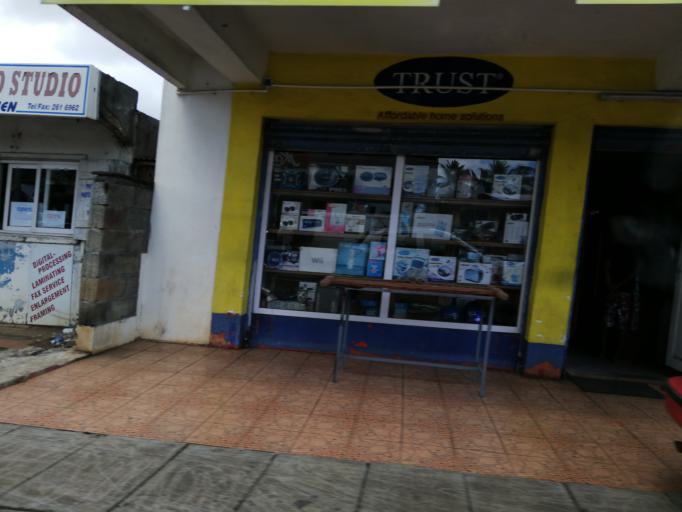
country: MU
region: Pamplemousses
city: Triolet
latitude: -20.0550
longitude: 57.5529
